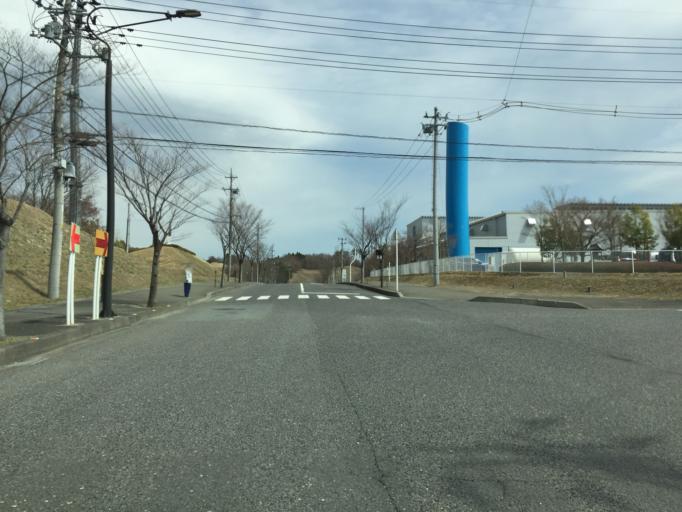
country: JP
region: Fukushima
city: Miharu
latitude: 37.4367
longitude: 140.5209
